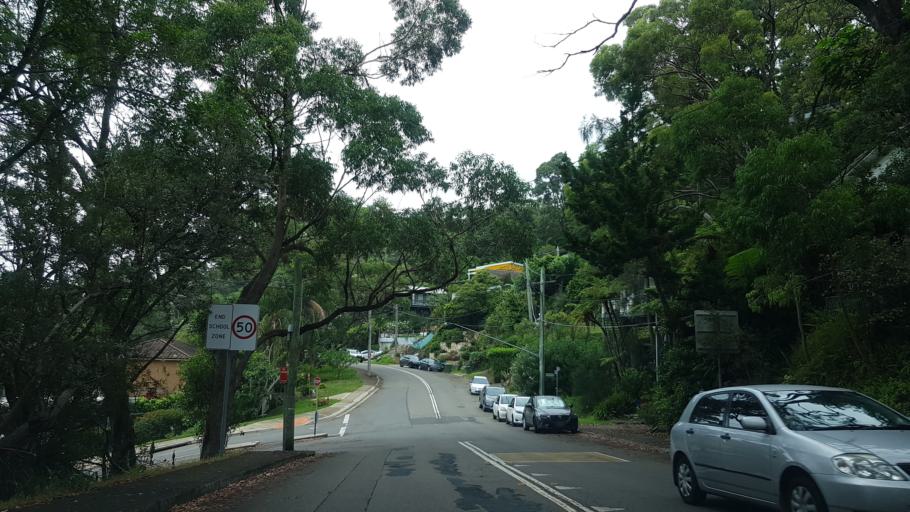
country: AU
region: New South Wales
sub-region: Pittwater
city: North Narrabeen
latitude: -33.7045
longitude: 151.2870
